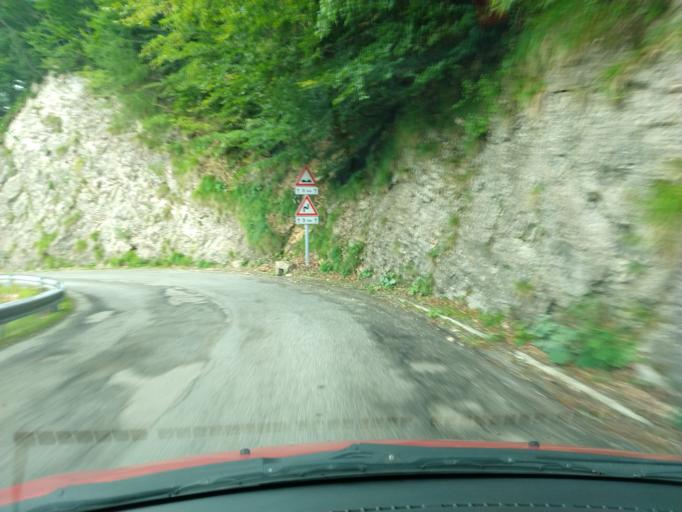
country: IT
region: Veneto
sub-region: Provincia di Vicenza
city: Tonezza del Cimone
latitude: 45.8756
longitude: 11.3259
